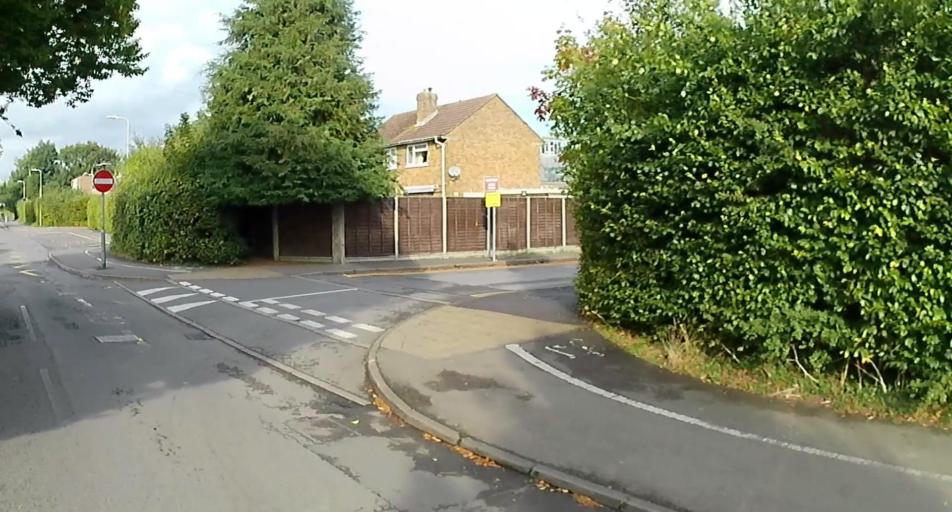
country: GB
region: England
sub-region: West Berkshire
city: Thatcham
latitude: 51.4009
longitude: -1.2496
